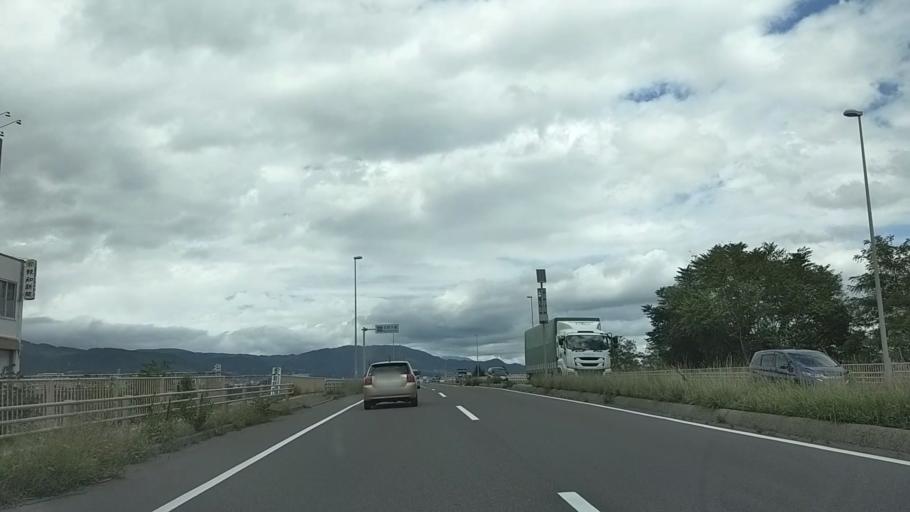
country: JP
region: Nagano
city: Nagano-shi
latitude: 36.6164
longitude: 138.1979
